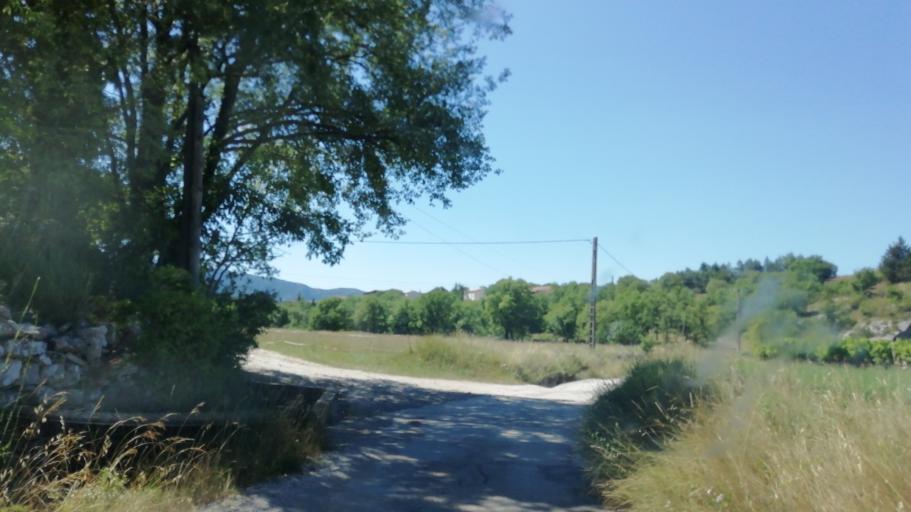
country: FR
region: Languedoc-Roussillon
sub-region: Departement de l'Herault
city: Saint-Martin-de-Londres
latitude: 43.8301
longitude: 3.7767
